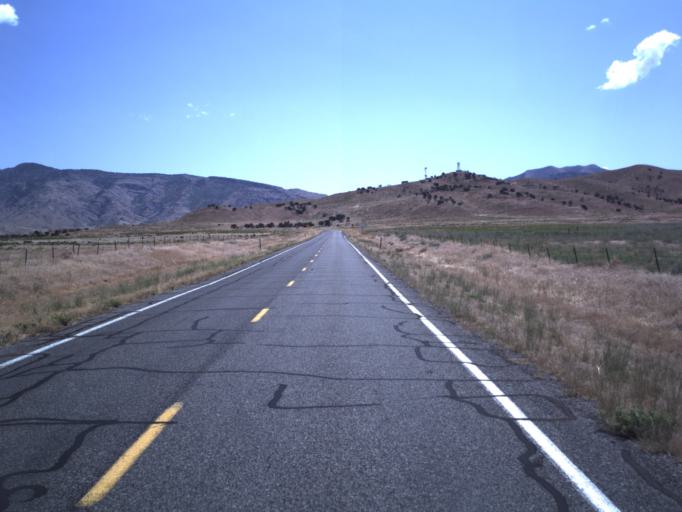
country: US
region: Utah
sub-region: Millard County
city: Delta
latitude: 39.3549
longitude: -112.3701
